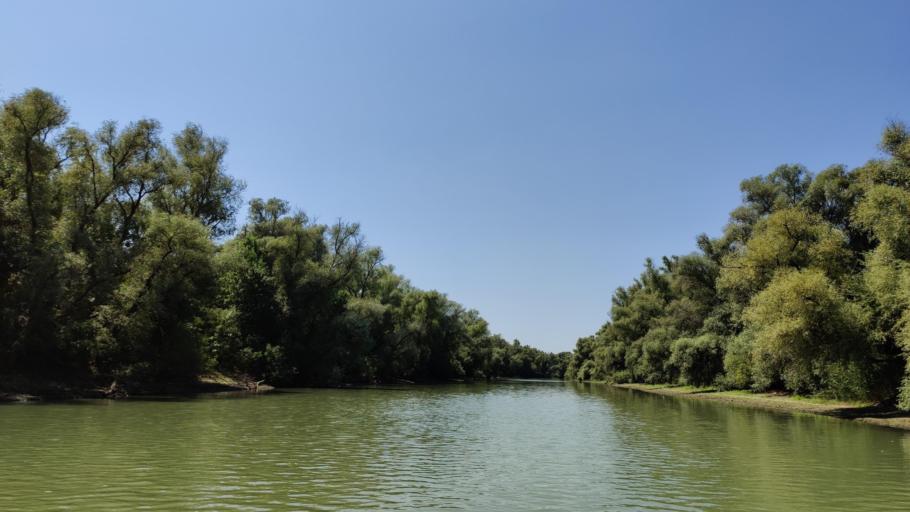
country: RO
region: Tulcea
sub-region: Comuna Nufaru
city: Nufaru
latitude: 45.2326
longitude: 28.9101
